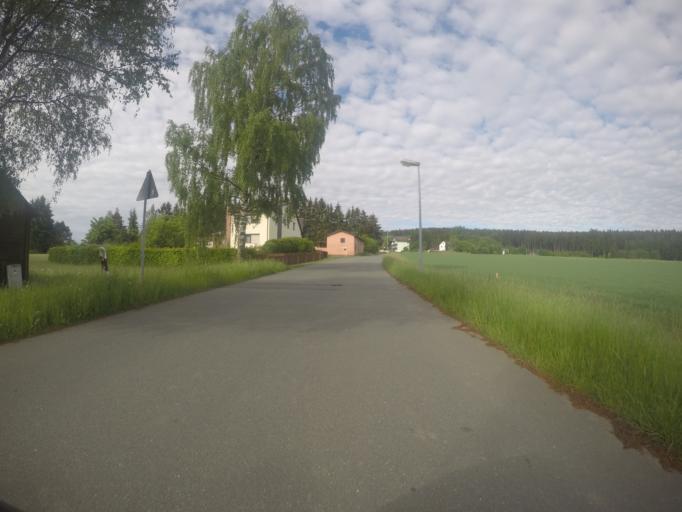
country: DE
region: Bavaria
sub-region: Upper Franconia
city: Schonwald
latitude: 50.2110
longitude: 12.0984
